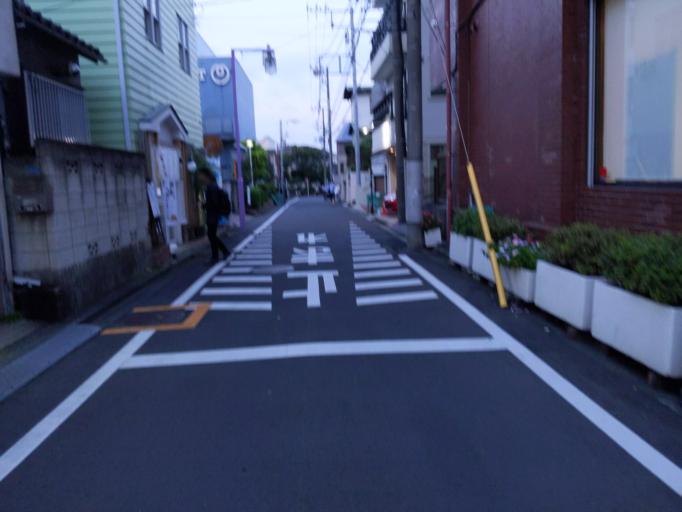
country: JP
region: Kanagawa
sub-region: Kawasaki-shi
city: Kawasaki
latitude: 35.5540
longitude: 139.6442
